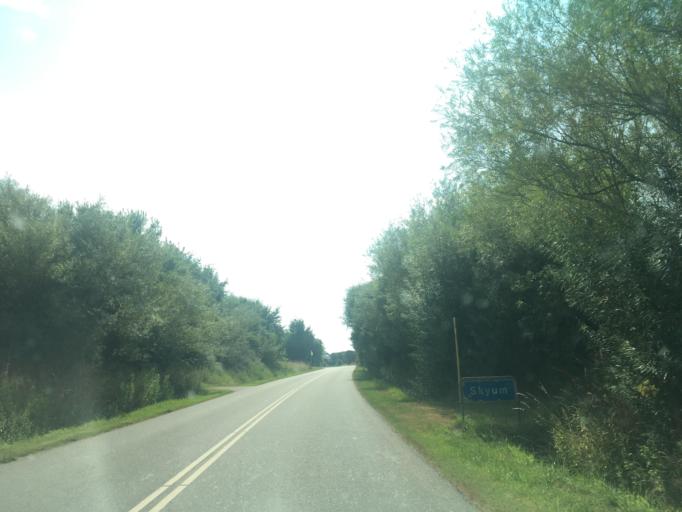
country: DK
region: North Denmark
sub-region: Thisted Kommune
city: Thisted
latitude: 56.8387
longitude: 8.5806
